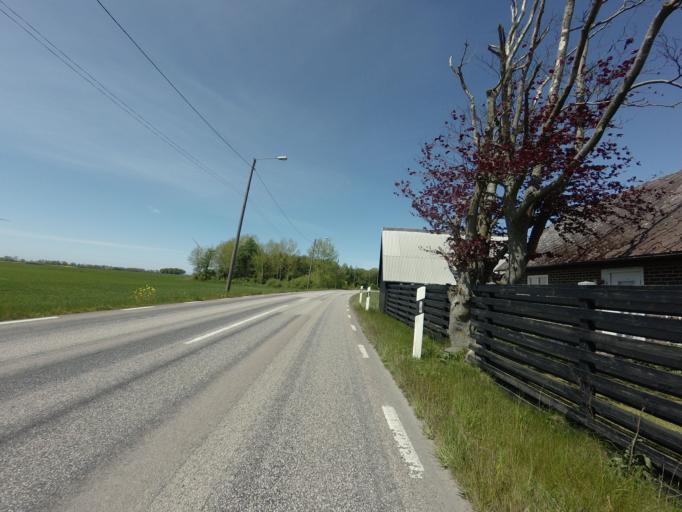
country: SE
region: Skane
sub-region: Helsingborg
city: Odakra
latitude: 56.1474
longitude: 12.6792
